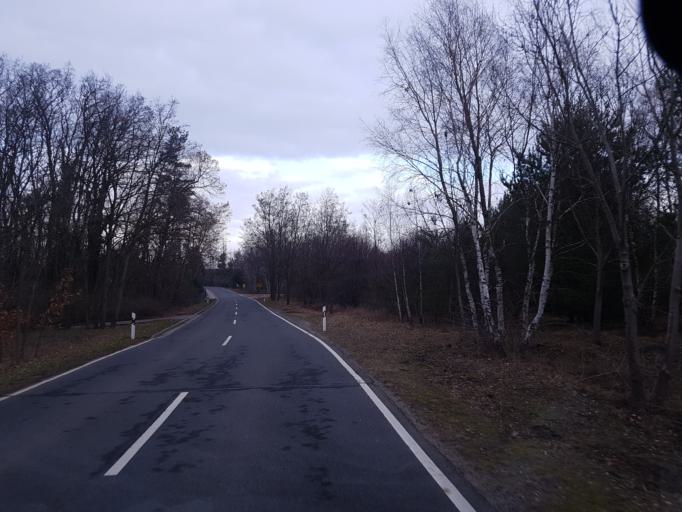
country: DE
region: Brandenburg
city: Sallgast
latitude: 51.5848
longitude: 13.8199
